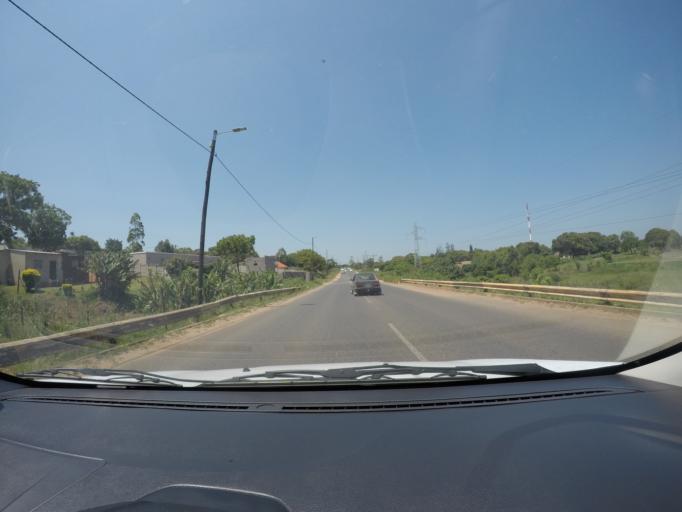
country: ZA
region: KwaZulu-Natal
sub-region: uThungulu District Municipality
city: eSikhawini
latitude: -28.8493
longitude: 31.9279
